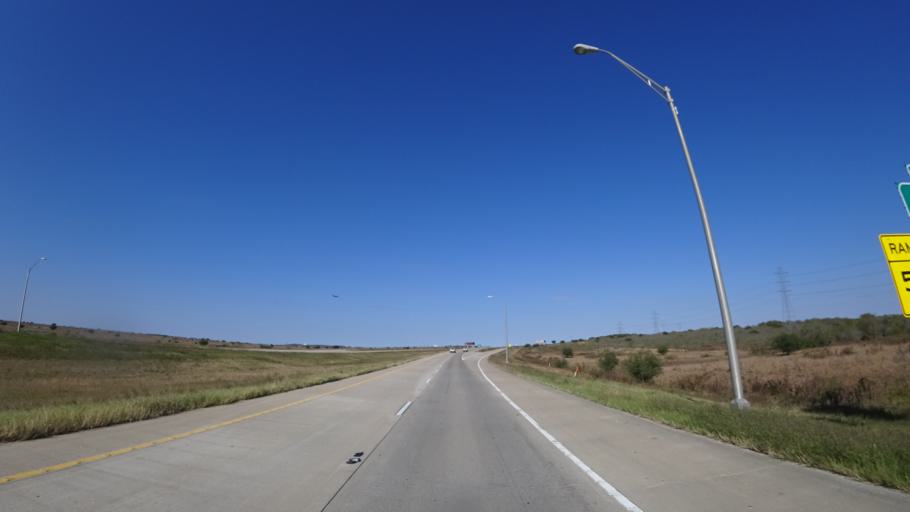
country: US
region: Texas
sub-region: Travis County
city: Onion Creek
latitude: 30.1293
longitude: -97.6641
